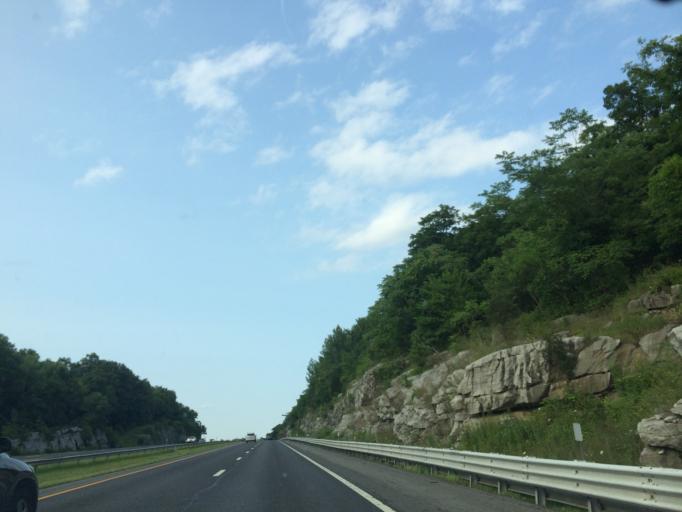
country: US
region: New York
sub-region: Ulster County
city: Saugerties
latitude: 42.0985
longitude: -73.9627
